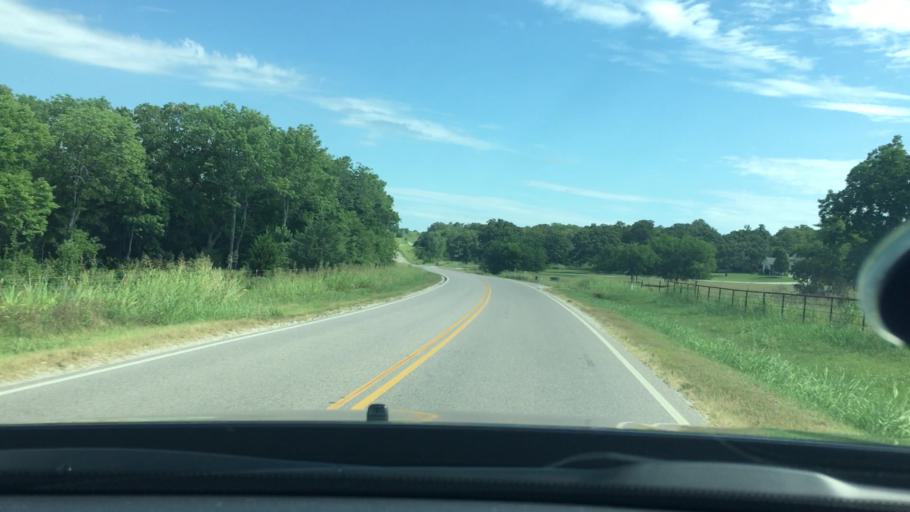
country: US
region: Oklahoma
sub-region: Pontotoc County
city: Ada
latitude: 34.7663
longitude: -96.5821
